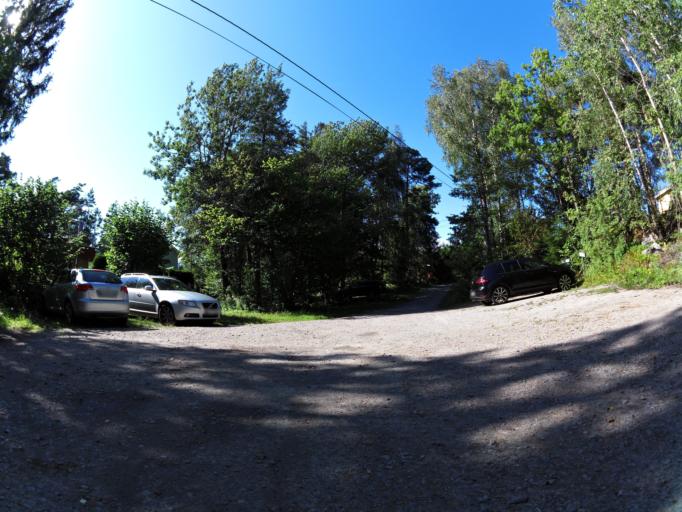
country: NO
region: Ostfold
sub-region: Fredrikstad
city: Fredrikstad
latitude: 59.1655
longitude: 10.8401
